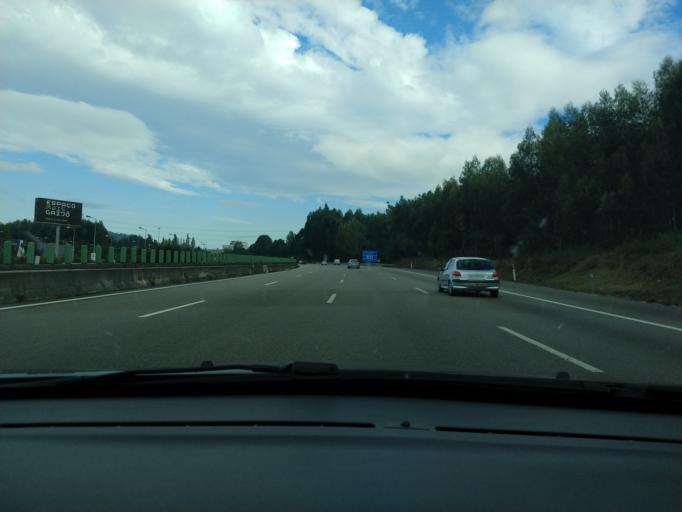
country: PT
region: Porto
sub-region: Vila Nova de Gaia
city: Grijo
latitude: 41.0373
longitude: -8.5707
